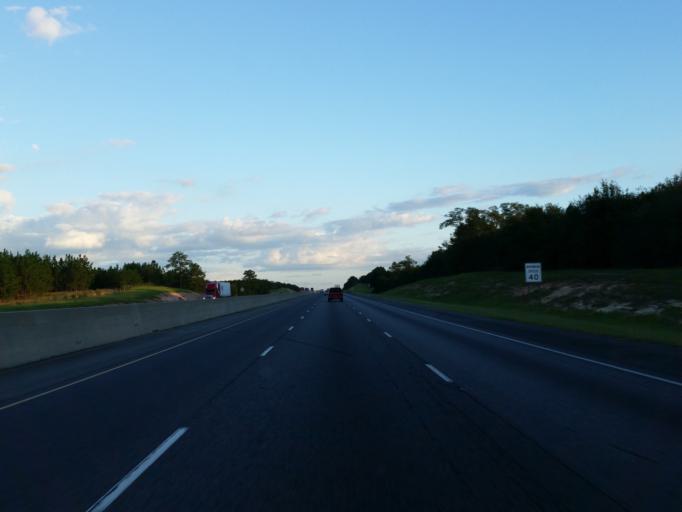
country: US
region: Georgia
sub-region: Turner County
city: Ashburn
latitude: 31.8004
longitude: -83.7013
